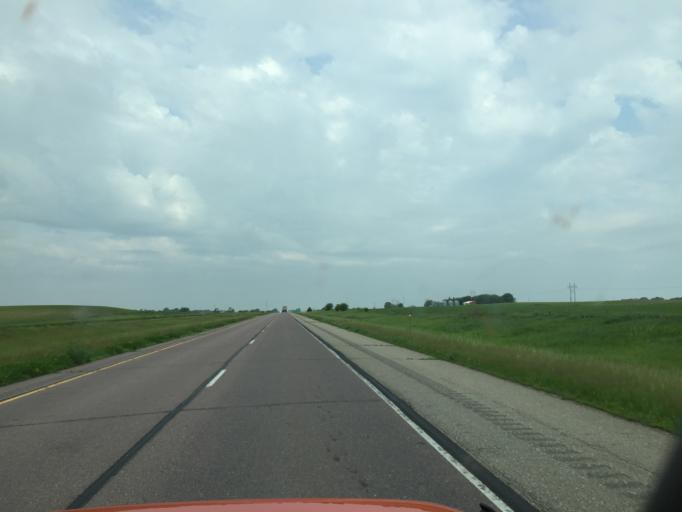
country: US
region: Minnesota
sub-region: Martin County
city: Fairmont
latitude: 43.6793
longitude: -94.4776
